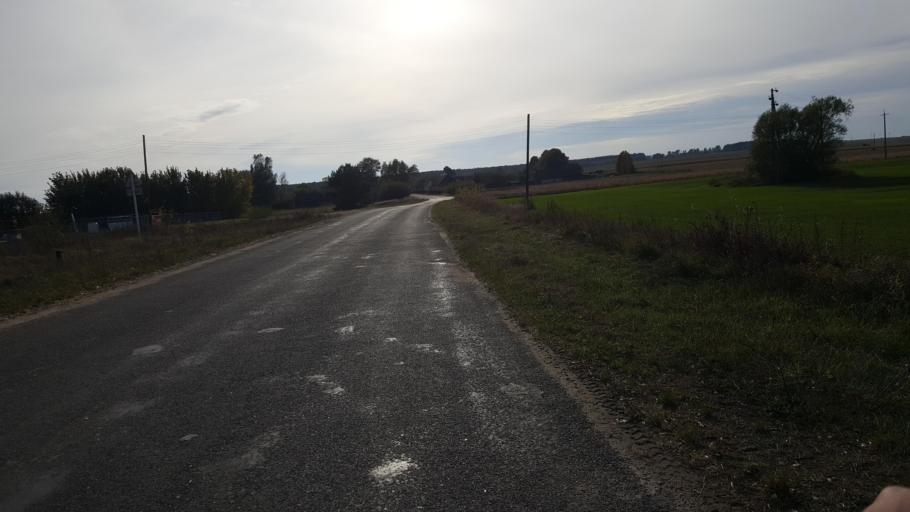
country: BY
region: Brest
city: Kamyanyets
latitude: 52.4079
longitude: 23.8909
